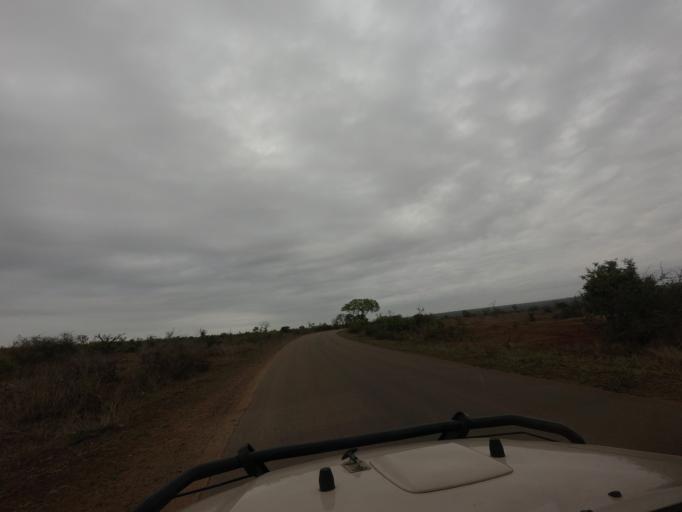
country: ZA
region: Mpumalanga
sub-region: Ehlanzeni District
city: Komatipoort
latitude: -25.3499
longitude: 31.8845
